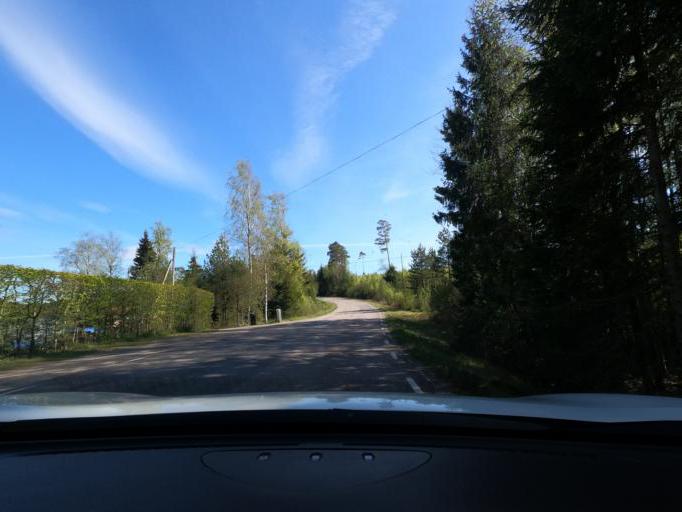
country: SE
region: Vaestra Goetaland
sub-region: Harryda Kommun
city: Hindas
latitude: 57.6687
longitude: 12.3531
